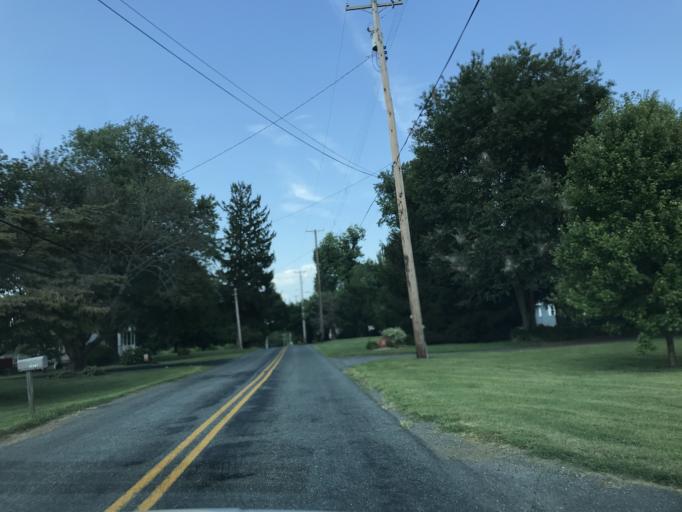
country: US
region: Maryland
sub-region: Harford County
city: South Bel Air
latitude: 39.6068
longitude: -76.3006
